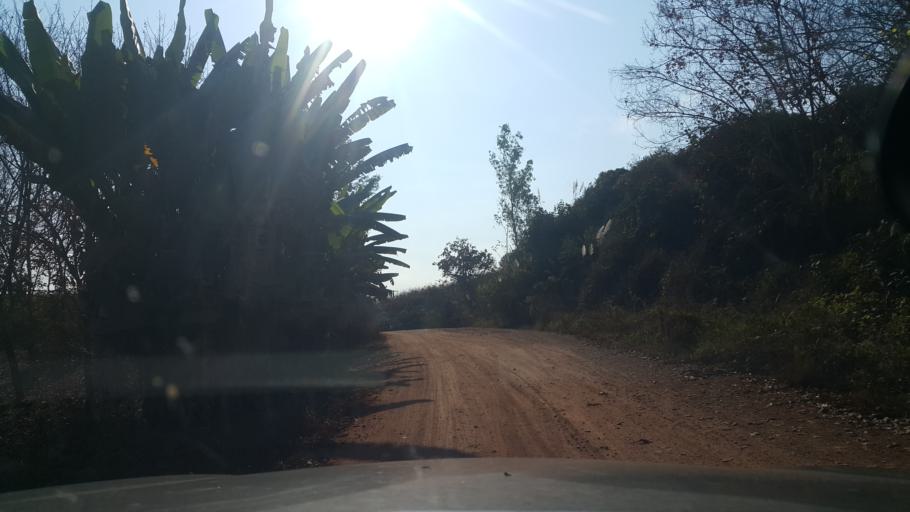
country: TH
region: Loei
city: Chiang Khan
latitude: 17.8103
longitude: 101.6180
